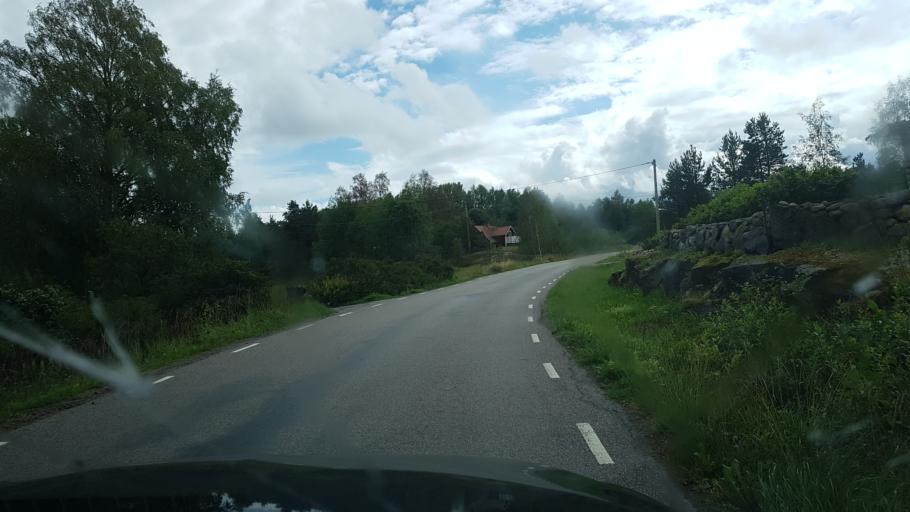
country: SE
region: Uppsala
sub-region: Osthammars Kommun
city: Oregrund
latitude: 60.3595
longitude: 18.4459
